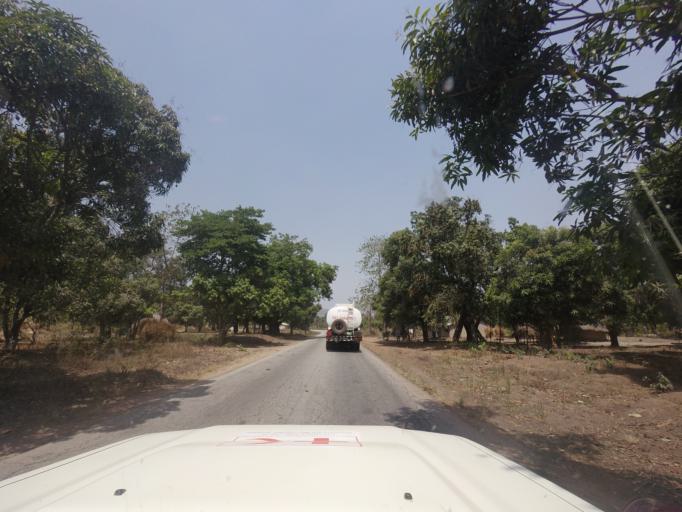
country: GN
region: Kindia
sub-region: Kindia
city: Kindia
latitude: 9.9008
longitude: -13.0254
